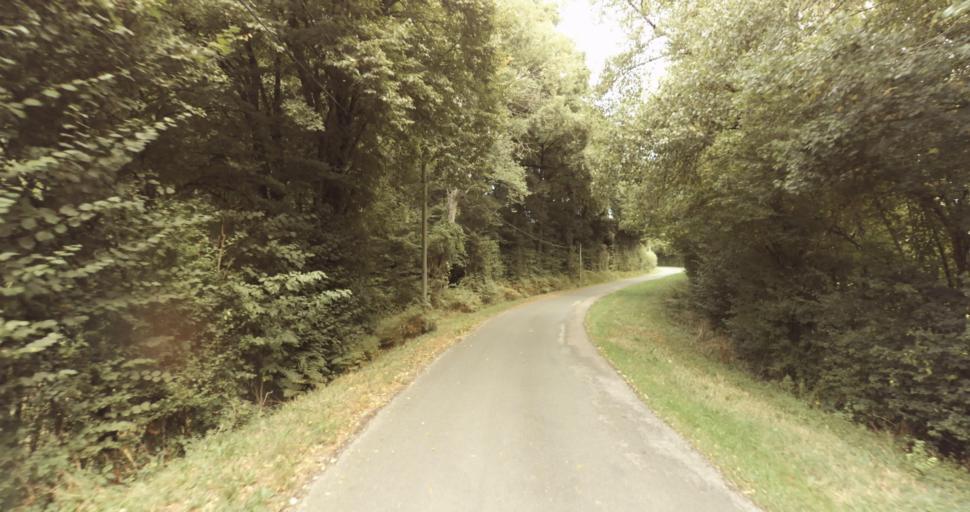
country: FR
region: Lower Normandy
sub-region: Departement du Calvados
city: Orbec
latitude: 48.9490
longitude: 0.3728
